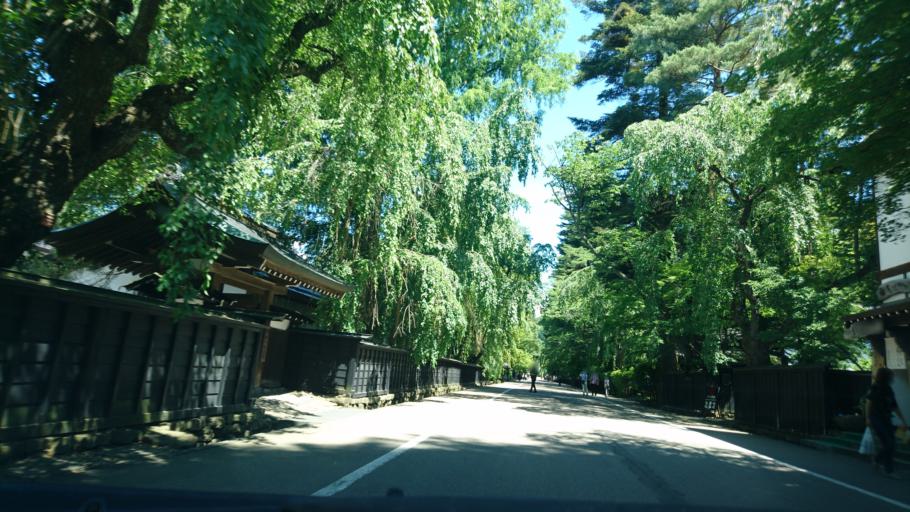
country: JP
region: Akita
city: Kakunodatemachi
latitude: 39.5993
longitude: 140.5616
